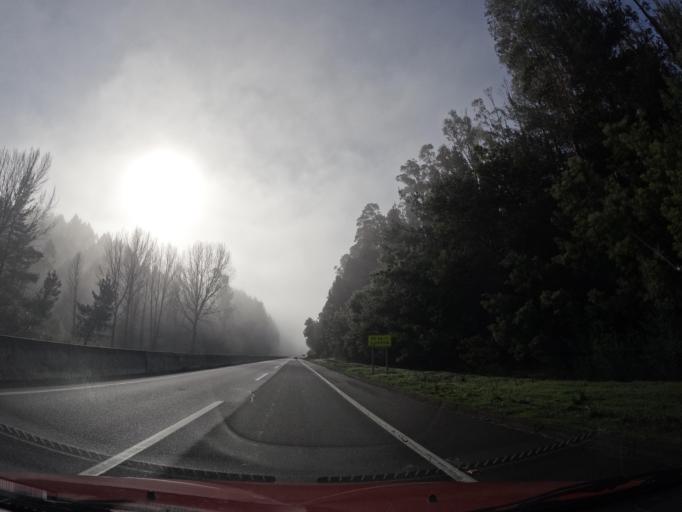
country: CL
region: Biobio
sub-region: Provincia de Concepcion
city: Penco
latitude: -36.7302
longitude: -72.8445
